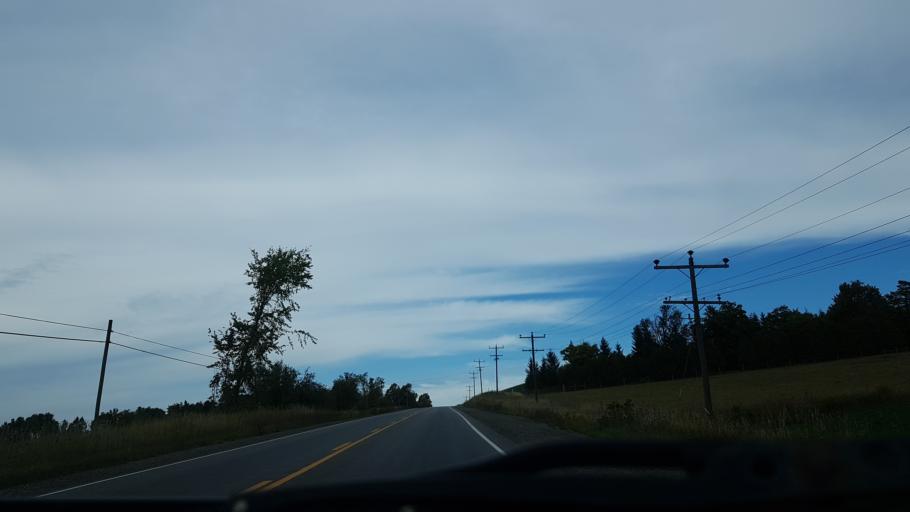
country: CA
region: Ontario
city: Wasaga Beach
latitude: 44.3554
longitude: -80.0822
